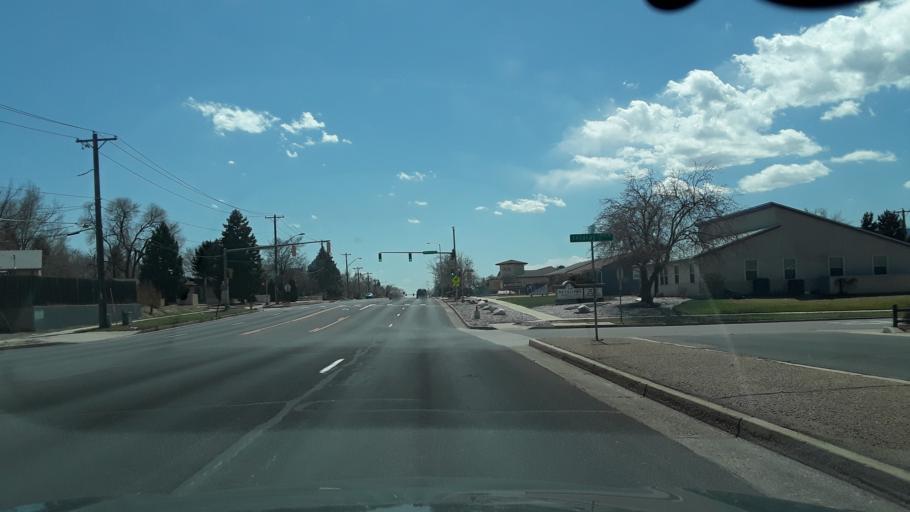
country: US
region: Colorado
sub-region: El Paso County
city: Colorado Springs
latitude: 38.8572
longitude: -104.7758
